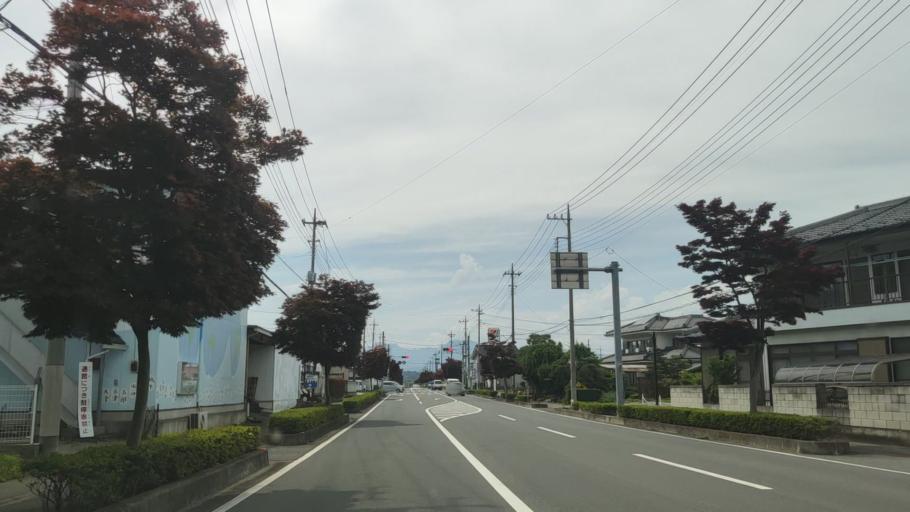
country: JP
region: Gunma
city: Tomioka
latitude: 36.2457
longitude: 138.8929
